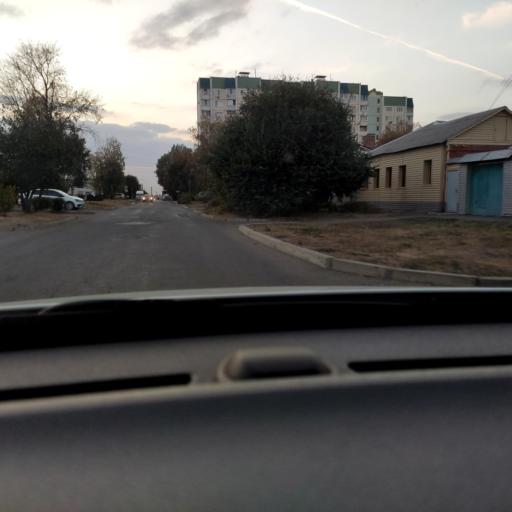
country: RU
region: Voronezj
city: Voronezh
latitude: 51.6909
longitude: 39.2140
